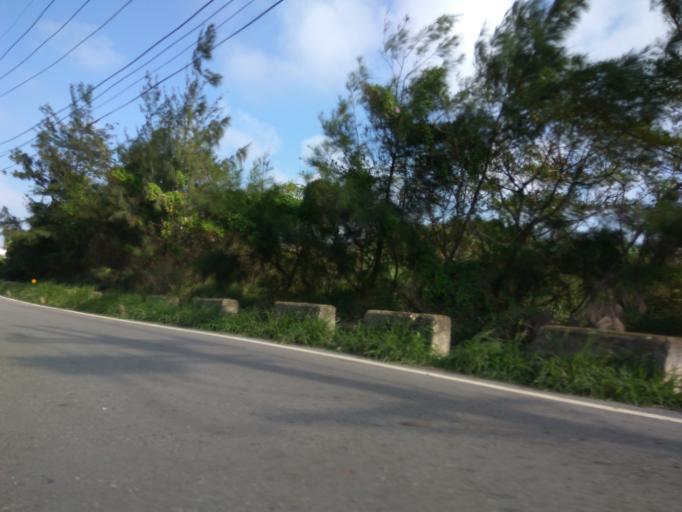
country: TW
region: Taiwan
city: Taoyuan City
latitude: 25.0736
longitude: 121.1730
